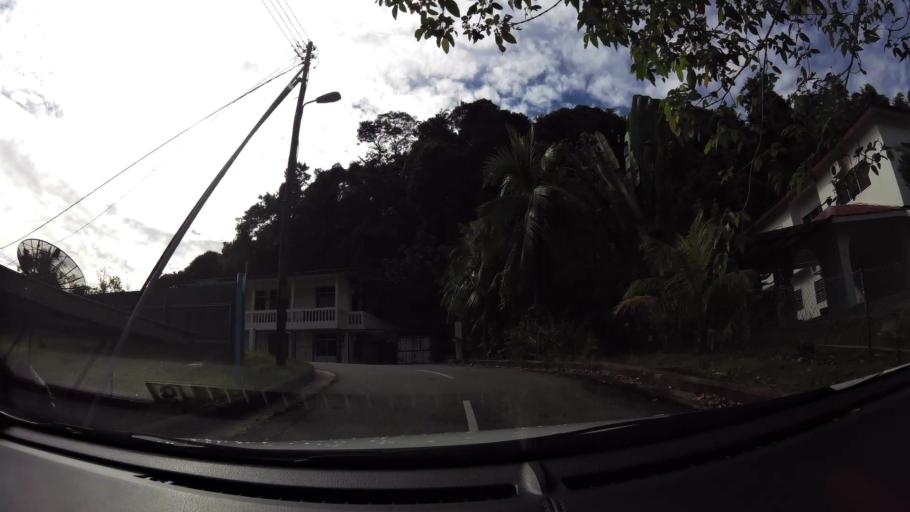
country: BN
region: Brunei and Muara
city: Bandar Seri Begawan
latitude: 4.8914
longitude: 114.9656
